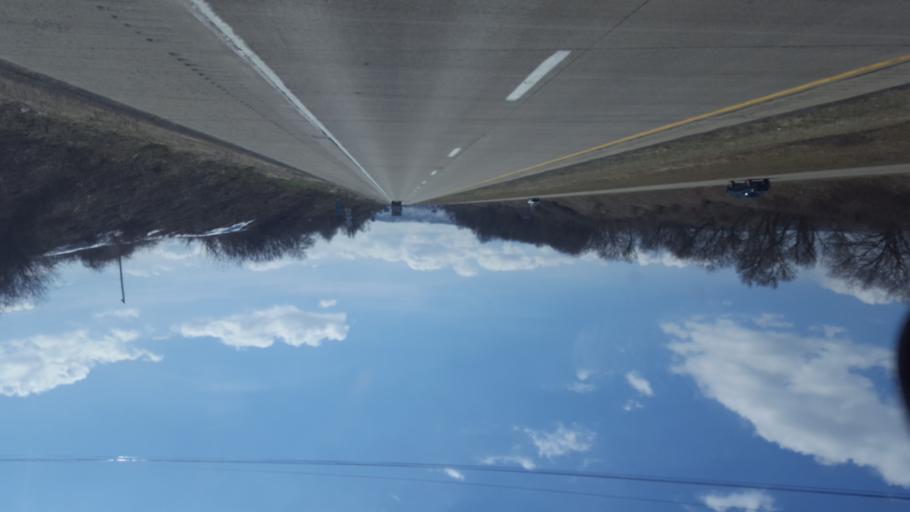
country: US
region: Pennsylvania
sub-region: Centre County
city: Bellefonte
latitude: 40.9066
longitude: -77.7405
